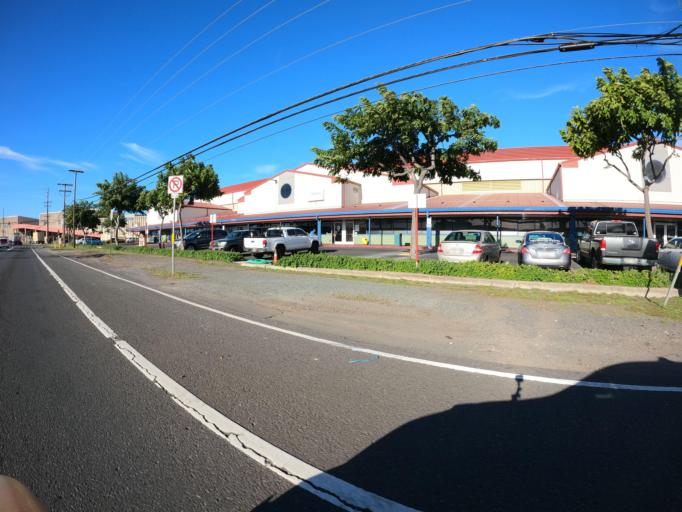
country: US
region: Hawaii
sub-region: Honolulu County
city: Honolulu
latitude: 21.3238
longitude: -157.8909
